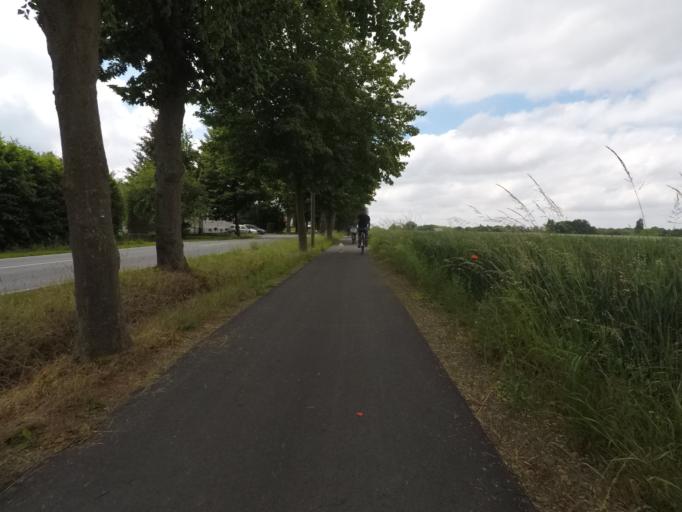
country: DE
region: North Rhine-Westphalia
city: Enger
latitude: 52.1321
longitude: 8.5275
